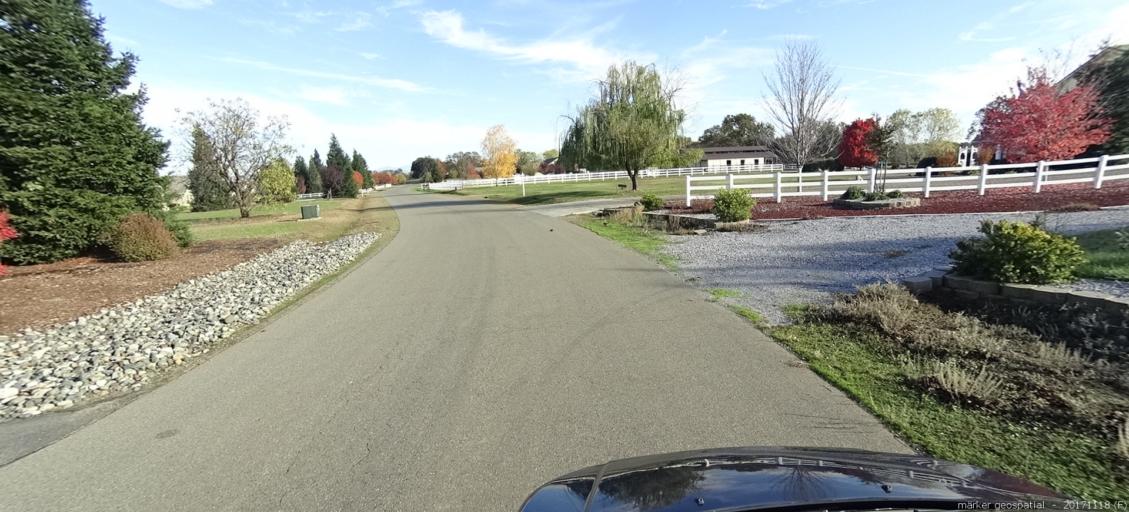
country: US
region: California
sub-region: Shasta County
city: Cottonwood
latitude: 40.3765
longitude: -122.3456
